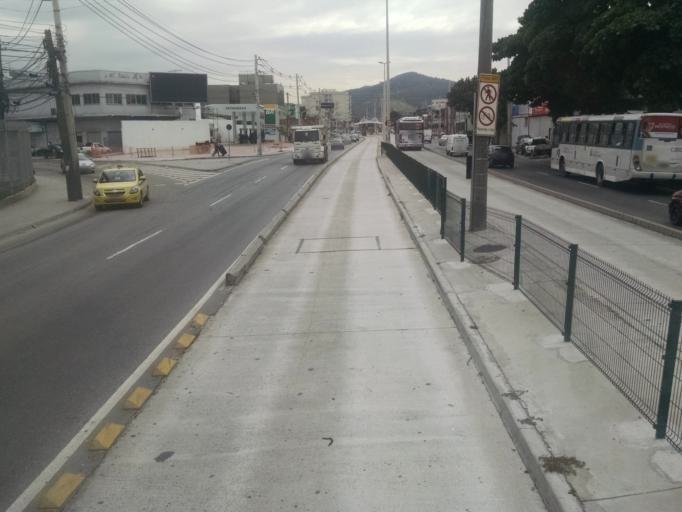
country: BR
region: Rio de Janeiro
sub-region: Sao Joao De Meriti
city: Sao Joao de Meriti
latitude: -22.9314
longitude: -43.3732
